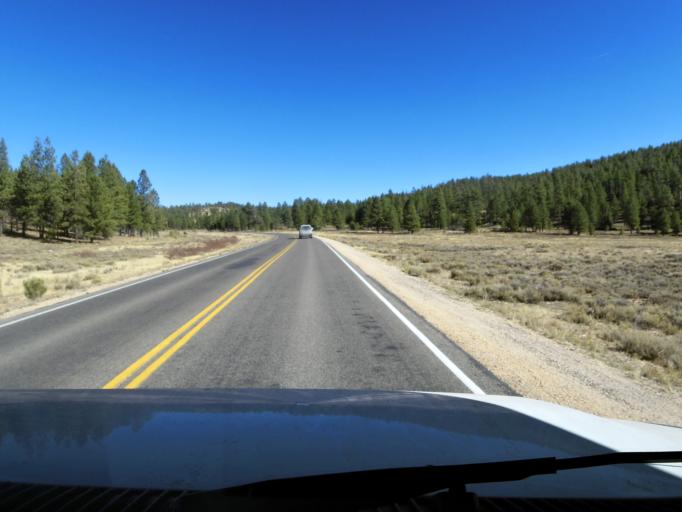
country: US
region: Utah
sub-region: Garfield County
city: Panguitch
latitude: 37.6070
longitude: -112.1887
